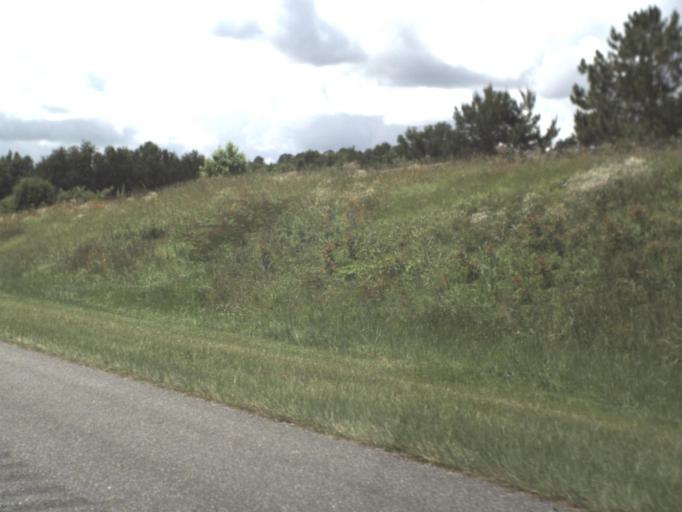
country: US
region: Florida
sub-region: Columbia County
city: Lake City
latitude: 30.1886
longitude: -82.6933
